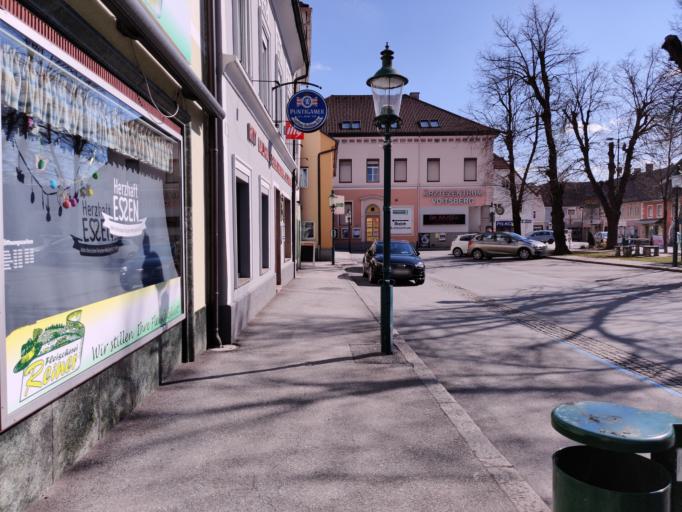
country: AT
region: Styria
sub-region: Politischer Bezirk Voitsberg
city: Voitsberg
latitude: 47.0494
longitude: 15.1512
